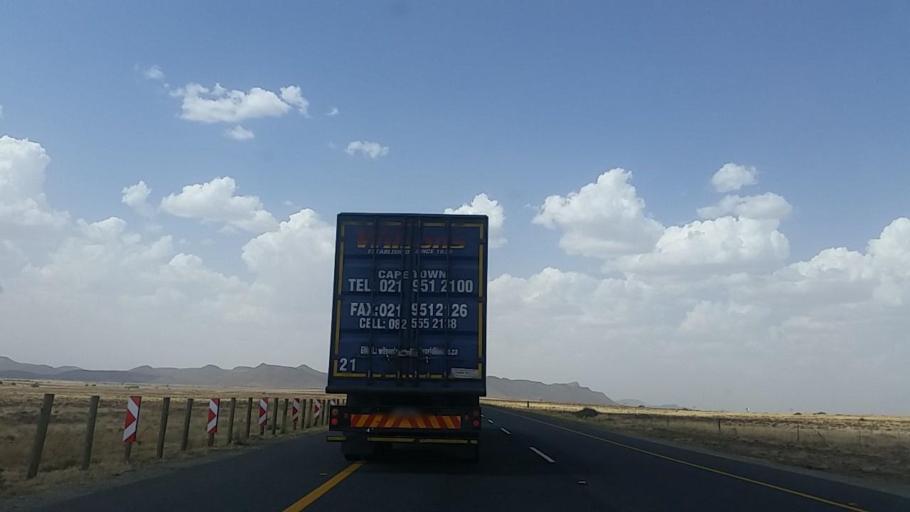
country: ZA
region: Northern Cape
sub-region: Pixley ka Seme District Municipality
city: Colesberg
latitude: -30.5673
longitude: 25.4638
